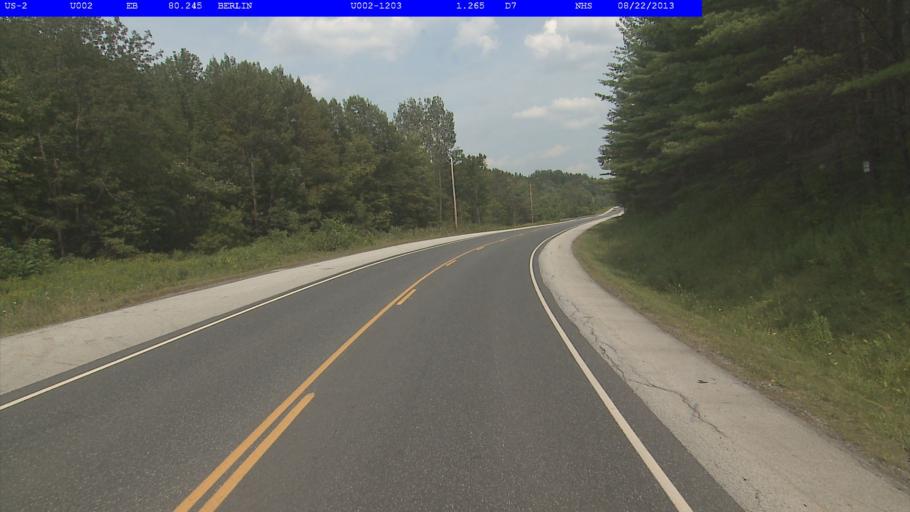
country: US
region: Vermont
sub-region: Washington County
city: Barre
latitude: 44.2399
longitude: -72.5214
